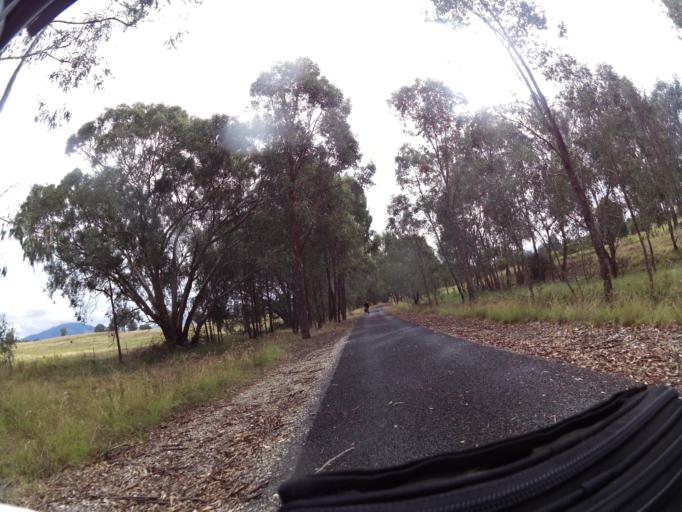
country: AU
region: New South Wales
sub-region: Albury Municipality
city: East Albury
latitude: -36.1435
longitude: 146.9996
